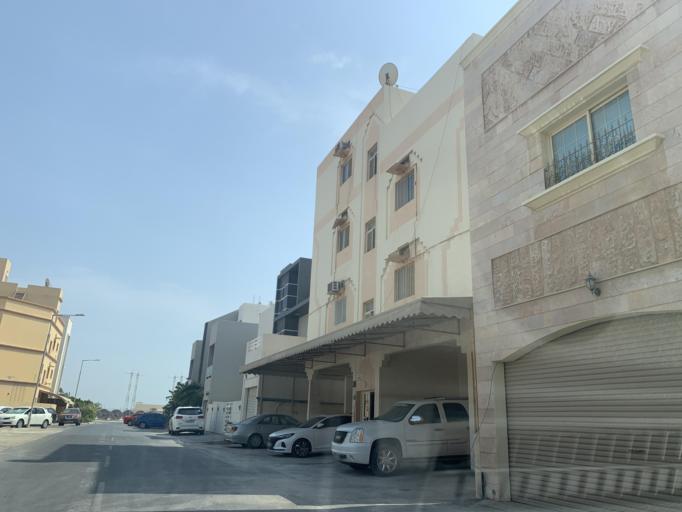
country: BH
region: Muharraq
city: Al Hadd
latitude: 26.2644
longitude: 50.6592
